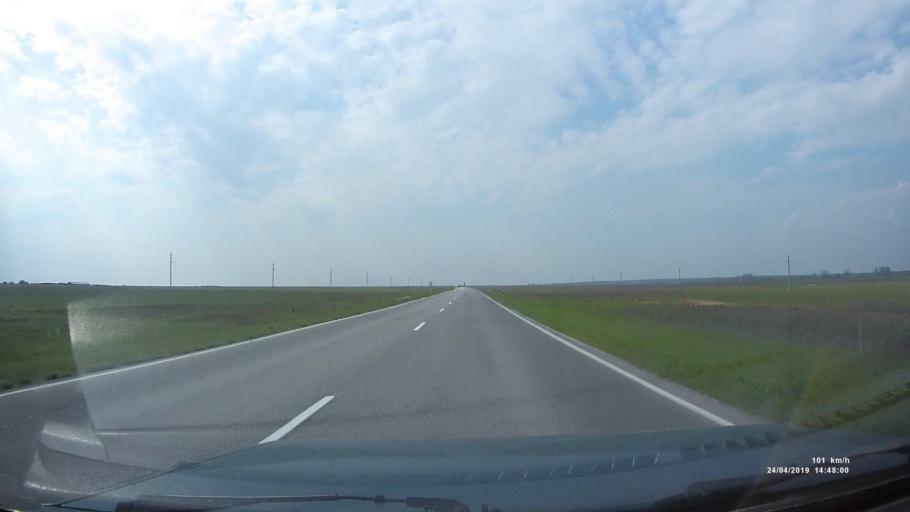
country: RU
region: Rostov
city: Remontnoye
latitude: 46.4968
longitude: 43.7632
